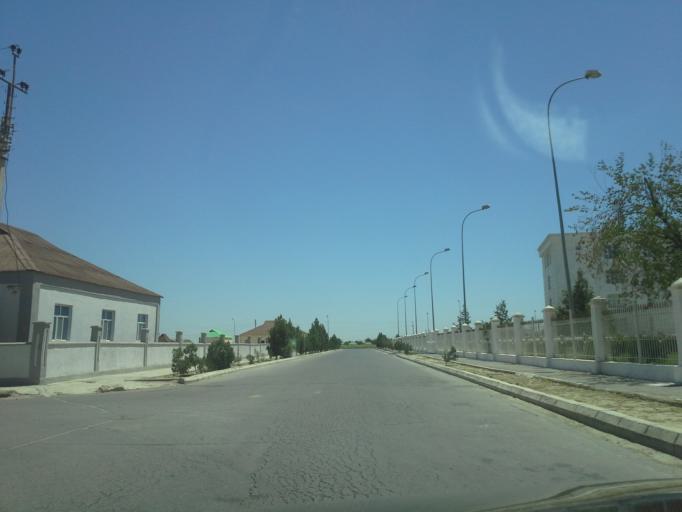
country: TM
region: Ahal
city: Abadan
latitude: 38.0364
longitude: 58.2689
